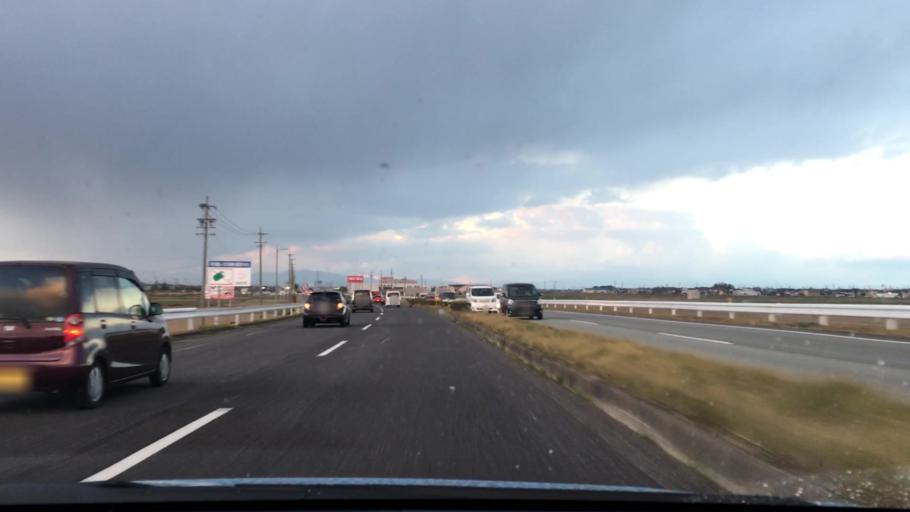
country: JP
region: Mie
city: Ise
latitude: 34.5518
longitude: 136.6560
